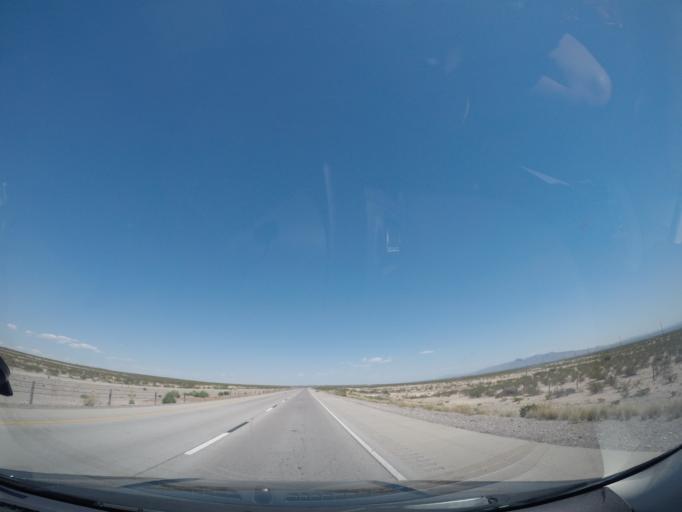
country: US
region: Texas
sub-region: El Paso County
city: Tornillo
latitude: 31.4781
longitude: -106.0709
